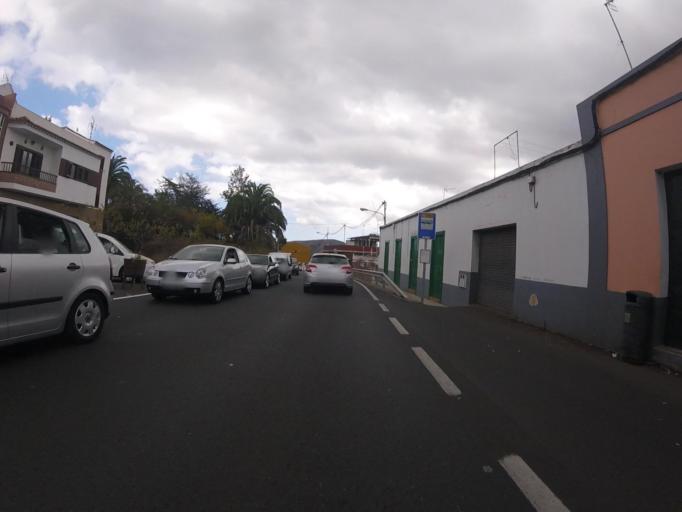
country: ES
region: Canary Islands
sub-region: Provincia de Las Palmas
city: Santa Brigida
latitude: 28.0213
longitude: -15.5170
